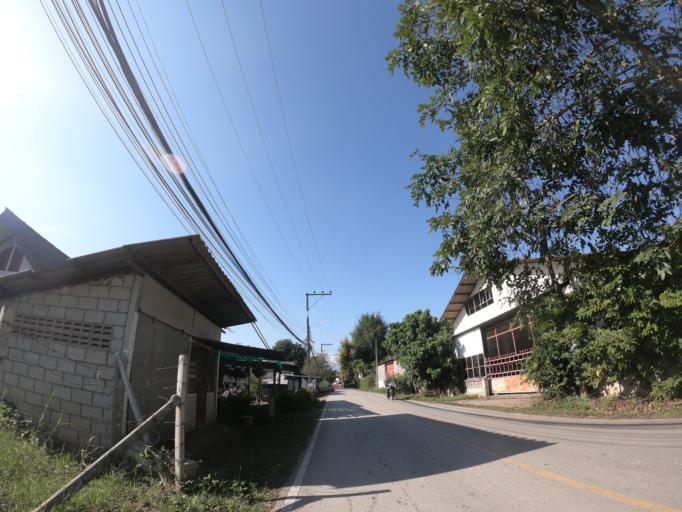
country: TH
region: Chiang Mai
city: Saraphi
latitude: 18.6994
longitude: 98.9931
